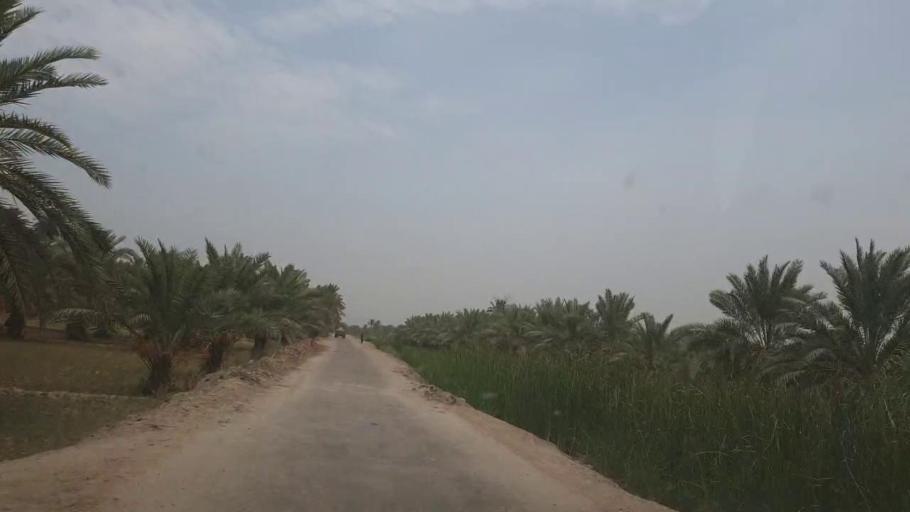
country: PK
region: Sindh
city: Kot Diji
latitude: 27.4289
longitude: 68.6965
